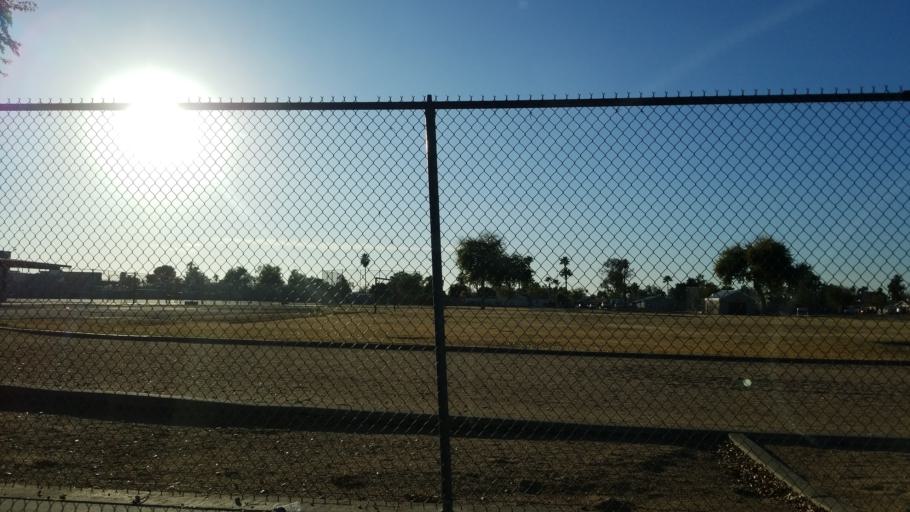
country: US
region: Arizona
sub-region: Maricopa County
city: Paradise Valley
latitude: 33.6501
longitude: -112.0201
